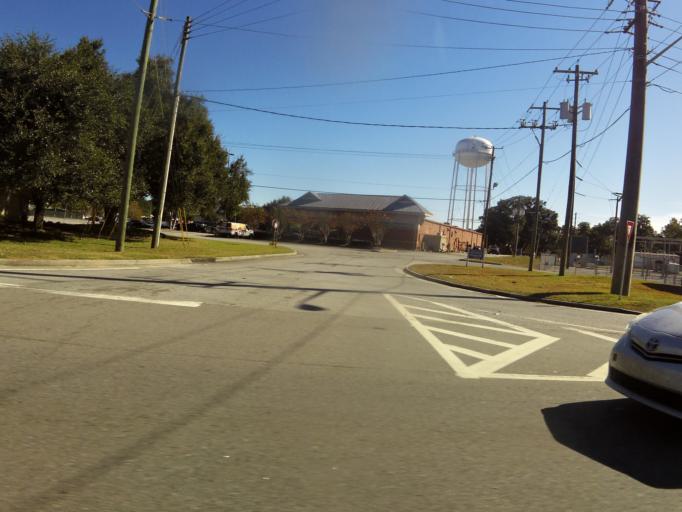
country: US
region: Georgia
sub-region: Bryan County
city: Richmond Hill
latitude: 31.9475
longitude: -81.3138
